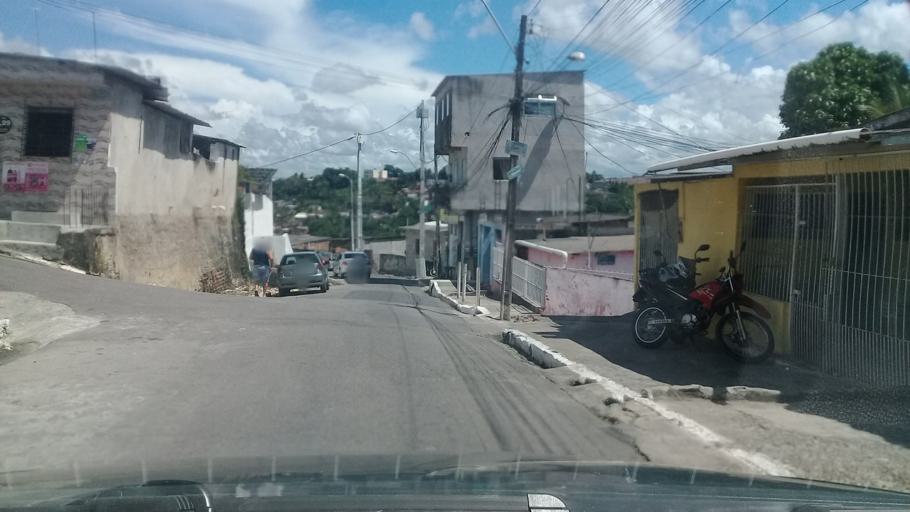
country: BR
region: Pernambuco
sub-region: Jaboatao Dos Guararapes
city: Jaboatao dos Guararapes
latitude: -8.1229
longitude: -34.9482
